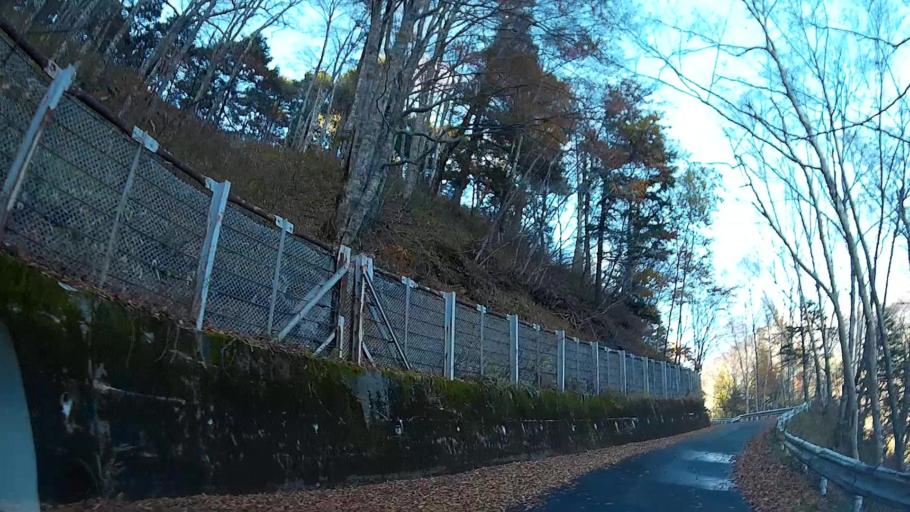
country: JP
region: Nagano
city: Hotaka
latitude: 36.2025
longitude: 137.5999
